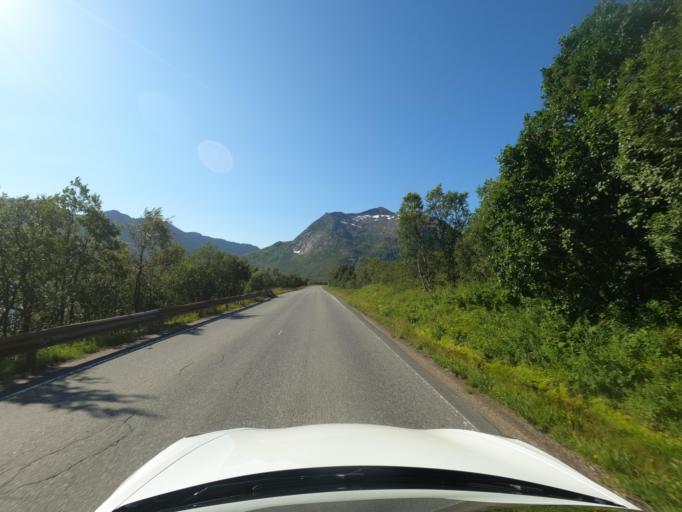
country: NO
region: Nordland
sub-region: Lodingen
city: Lodingen
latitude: 68.5488
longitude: 15.7454
